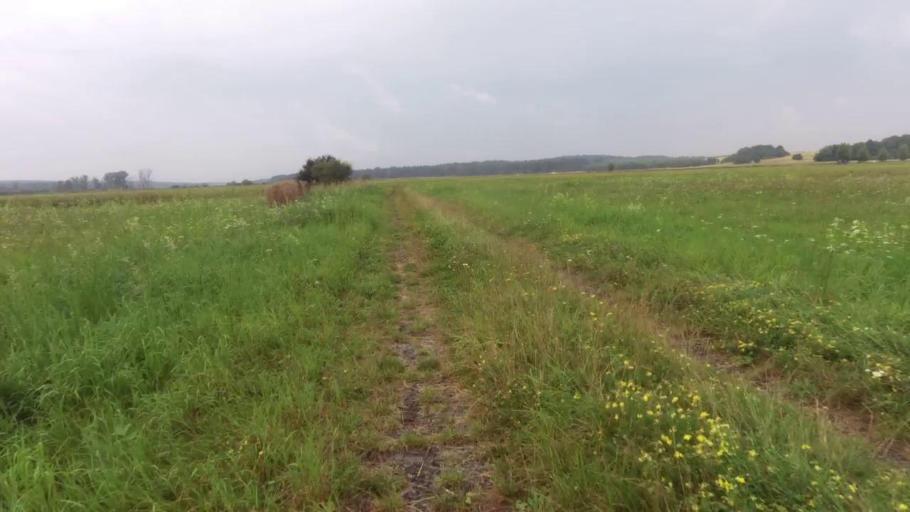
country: PL
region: West Pomeranian Voivodeship
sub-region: Powiat stargardzki
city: Suchan
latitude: 53.2513
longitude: 15.3968
